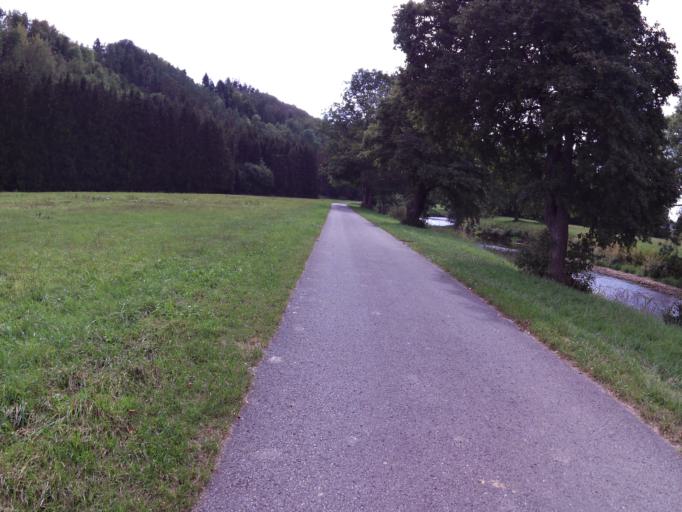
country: DE
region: Baden-Wuerttemberg
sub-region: Freiburg Region
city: Sulz am Neckar
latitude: 48.3723
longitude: 8.6574
